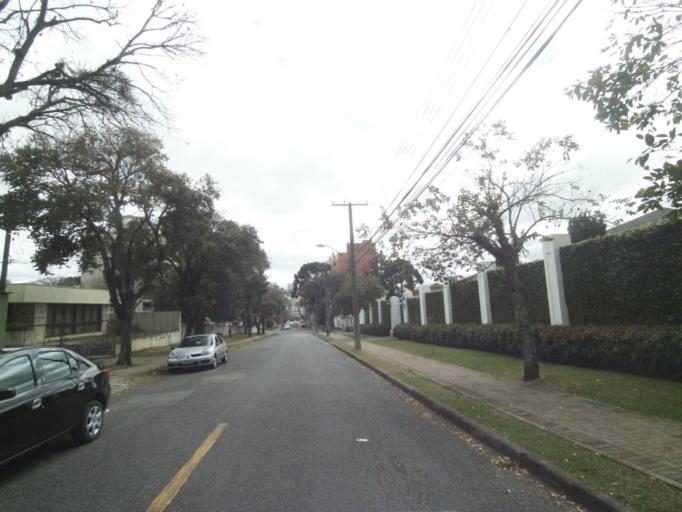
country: BR
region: Parana
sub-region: Curitiba
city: Curitiba
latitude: -25.4651
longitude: -49.2800
